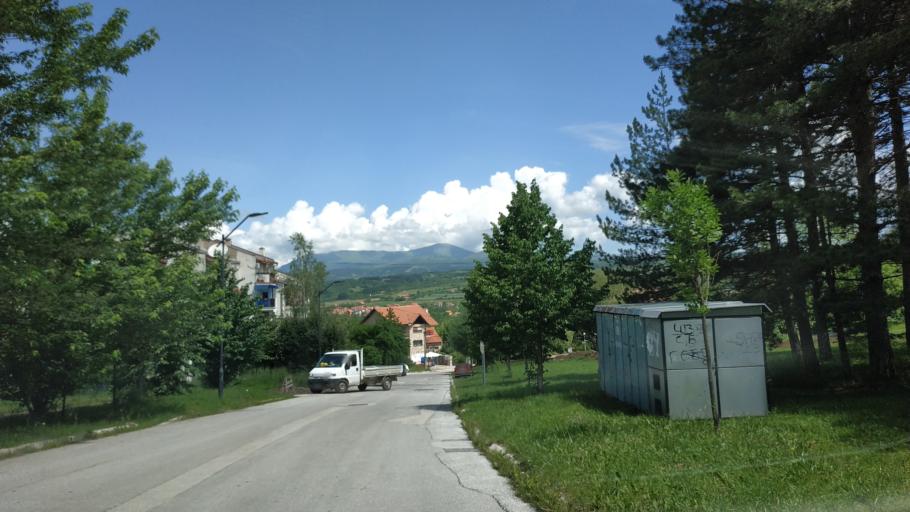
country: RS
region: Central Serbia
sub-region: Zajecarski Okrug
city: Soko Banja
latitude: 43.6400
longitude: 21.8704
